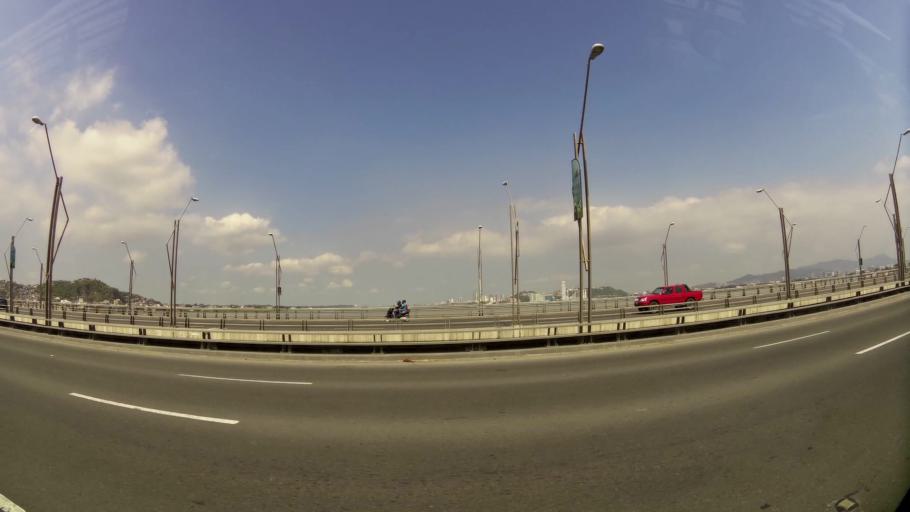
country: EC
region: Guayas
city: Eloy Alfaro
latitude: -2.1590
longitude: -79.8541
